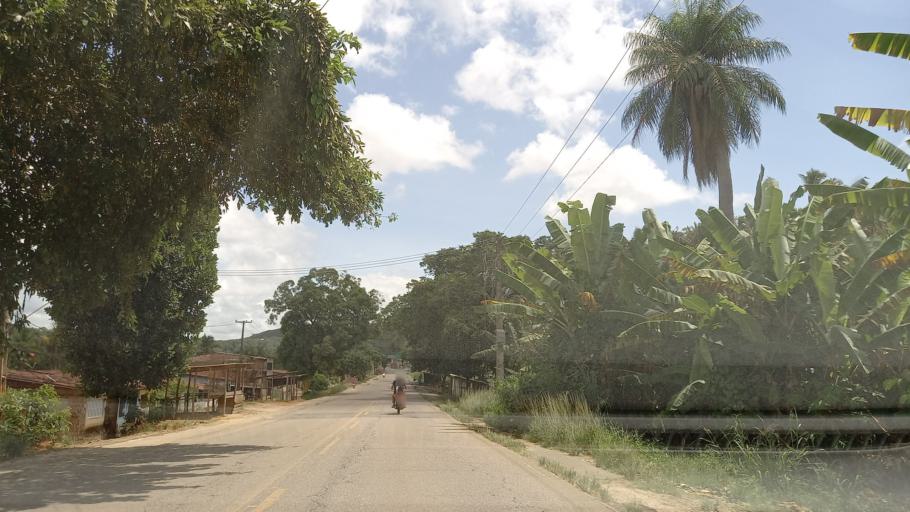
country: BR
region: Pernambuco
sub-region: Rio Formoso
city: Rio Formoso
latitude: -8.6562
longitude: -35.1502
